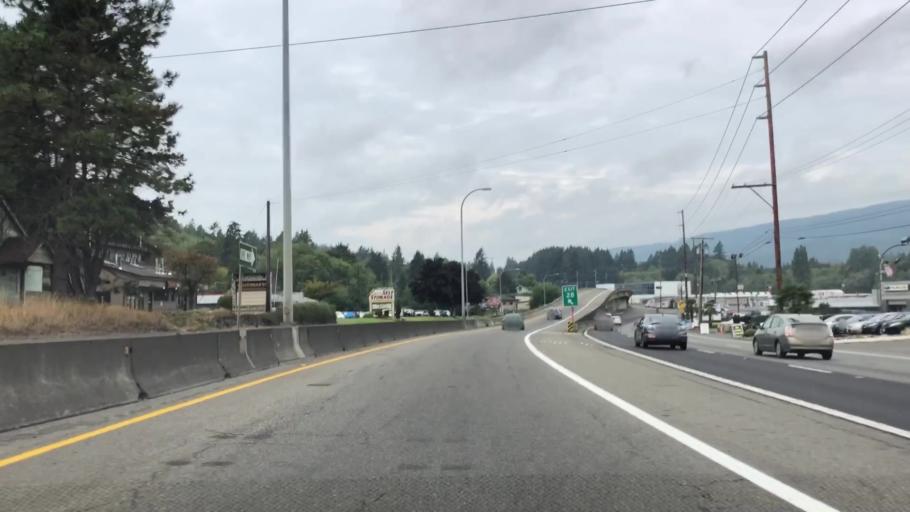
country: US
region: Washington
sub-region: Kitsap County
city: Navy Yard City
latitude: 47.5245
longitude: -122.6953
